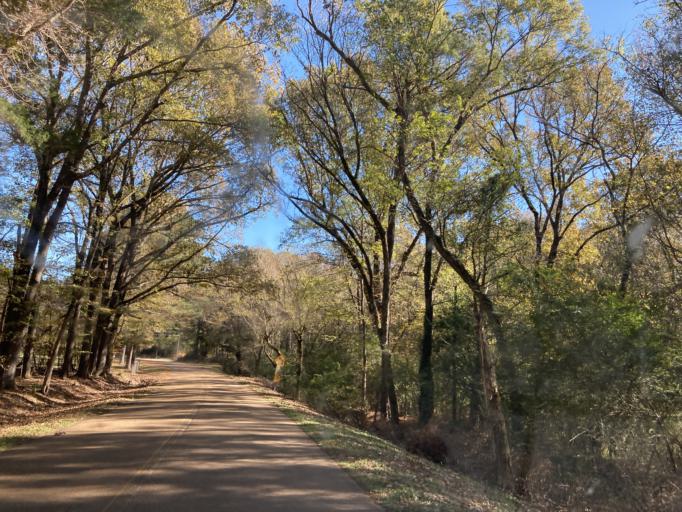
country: US
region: Mississippi
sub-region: Hinds County
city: Lynchburg
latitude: 32.5809
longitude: -90.5662
